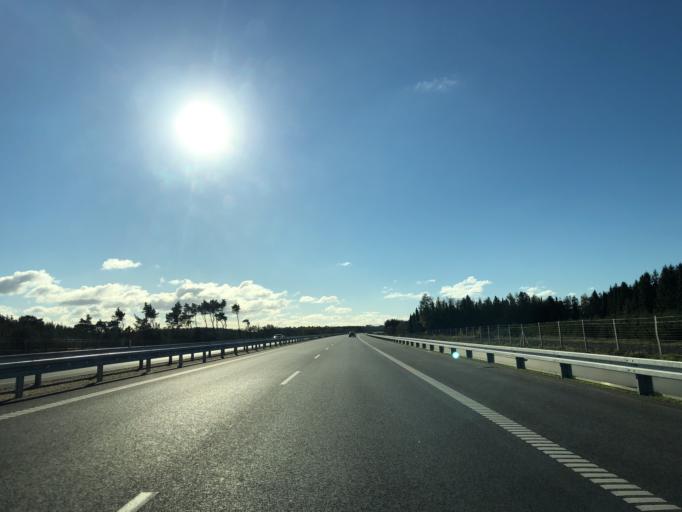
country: DK
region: Central Jutland
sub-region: Herning Kommune
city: Avlum
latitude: 56.3328
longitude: 8.7367
